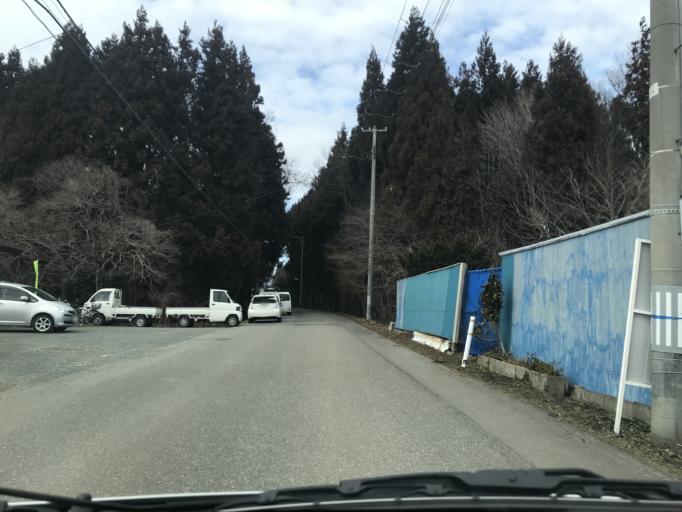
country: JP
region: Iwate
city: Kitakami
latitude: 39.3333
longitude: 140.9841
